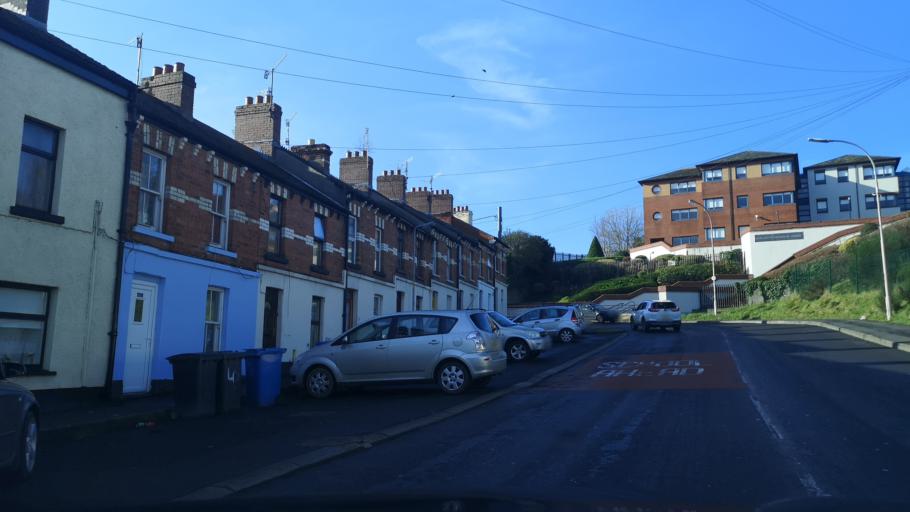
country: GB
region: Northern Ireland
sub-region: Newry and Mourne District
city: Newry
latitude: 54.1806
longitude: -6.3401
